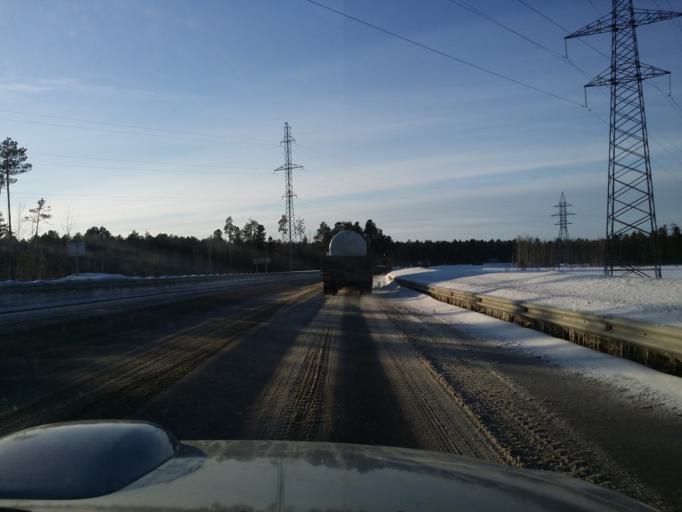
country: RU
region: Khanty-Mansiyskiy Avtonomnyy Okrug
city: Izluchinsk
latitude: 60.9358
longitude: 76.8691
